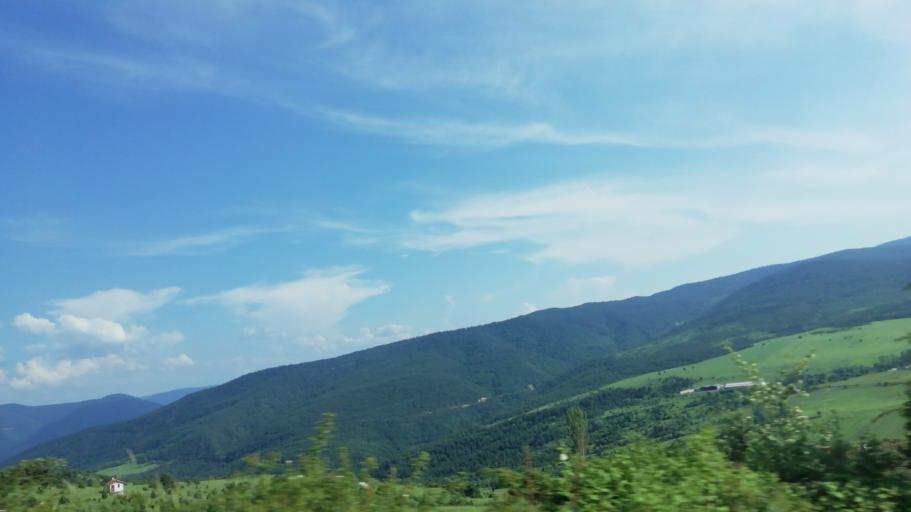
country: TR
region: Karabuk
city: Karabuk
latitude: 41.1076
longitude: 32.6024
